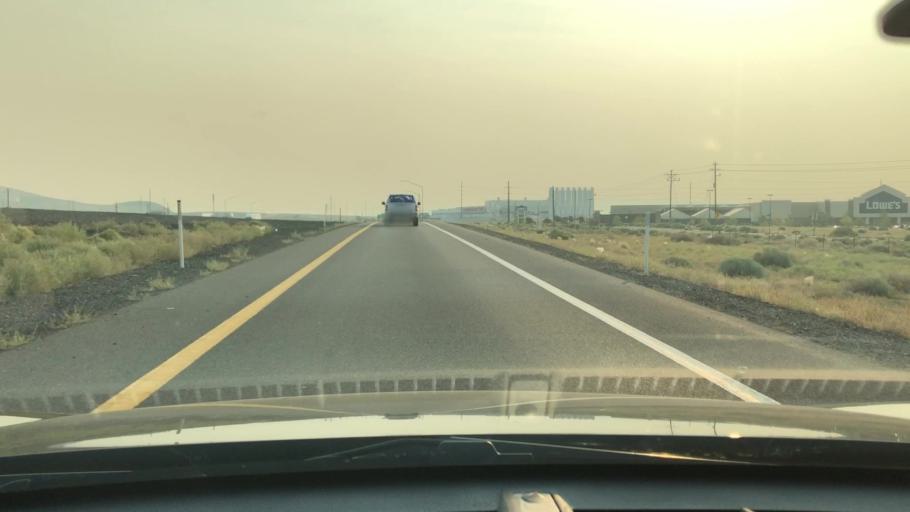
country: US
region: Nevada
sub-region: Lyon County
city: Fernley
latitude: 39.6134
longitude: -119.2155
